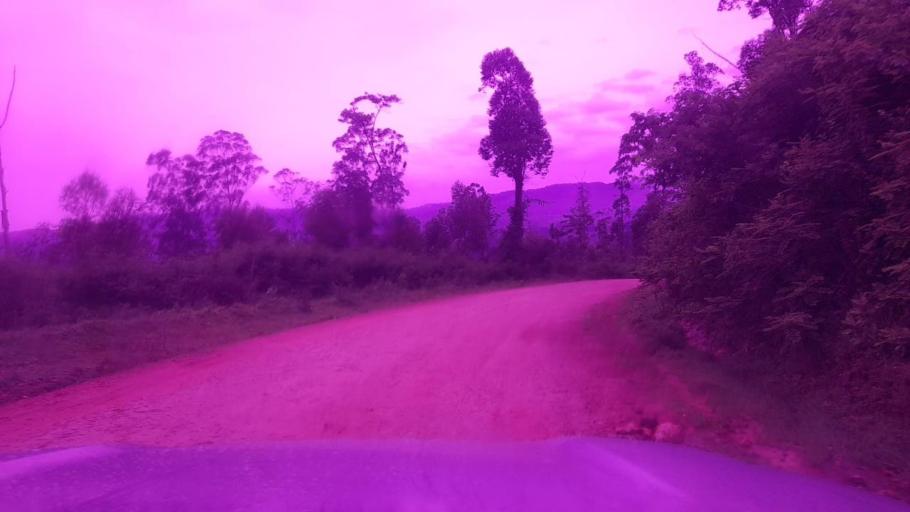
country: ET
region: Southern Nations, Nationalities, and People's Region
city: Bonga
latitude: 7.4492
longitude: 36.1422
